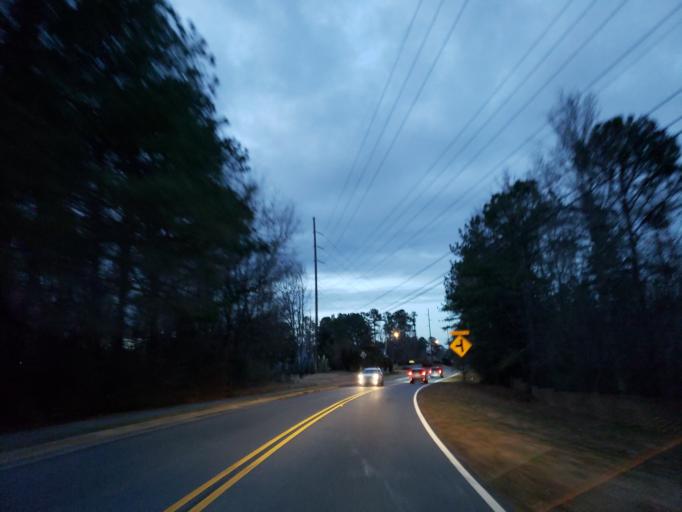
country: US
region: Georgia
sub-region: Cobb County
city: Kennesaw
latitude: 33.9854
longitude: -84.6723
